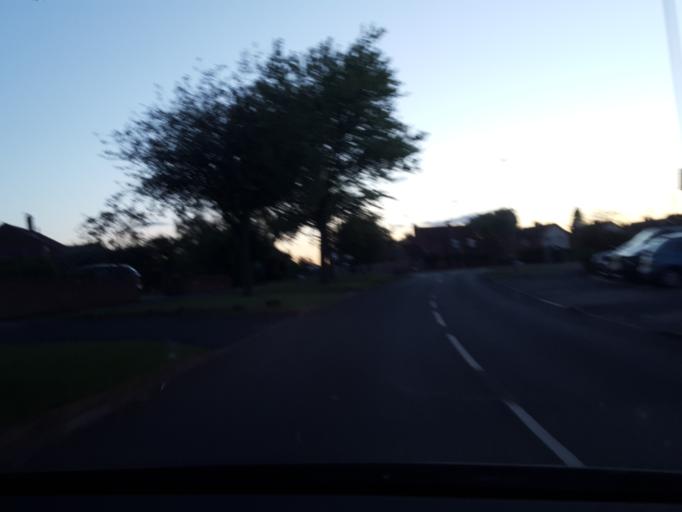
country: GB
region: England
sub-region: Leicestershire
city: Loughborough
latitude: 52.7523
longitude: -1.2167
